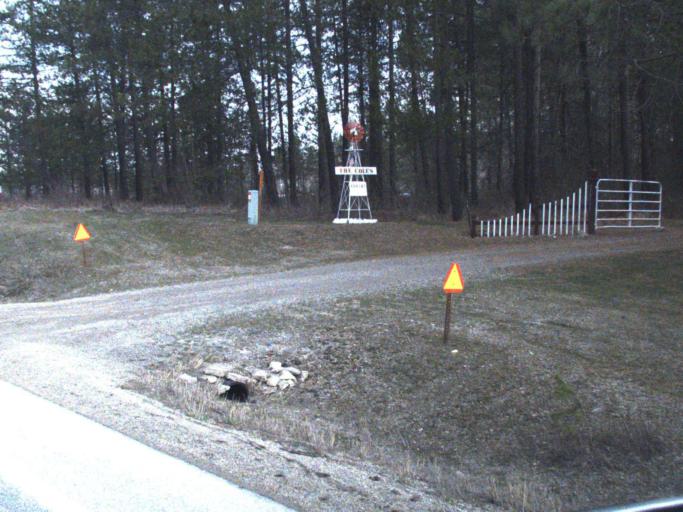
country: US
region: Washington
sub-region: Pend Oreille County
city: Newport
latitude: 48.2570
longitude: -117.2485
